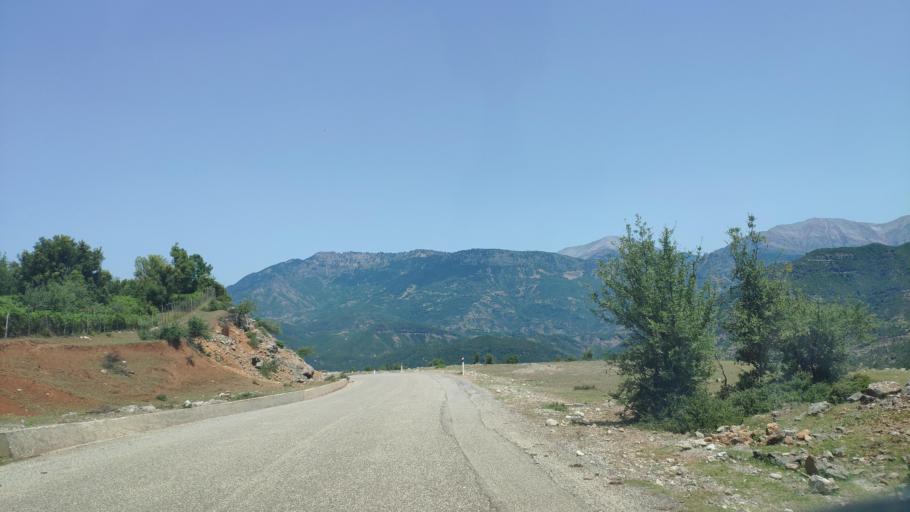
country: GR
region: Thessaly
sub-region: Nomos Kardhitsas
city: Anthiro
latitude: 39.1363
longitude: 21.3897
